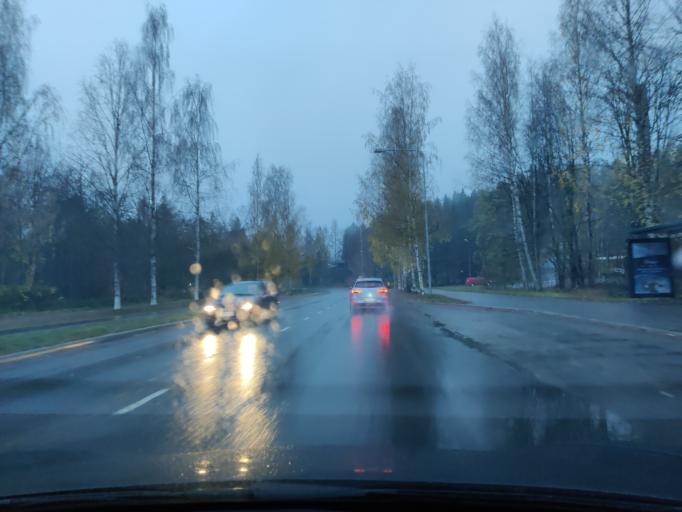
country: FI
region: Northern Savo
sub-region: Kuopio
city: Kuopio
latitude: 62.8503
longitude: 27.6407
